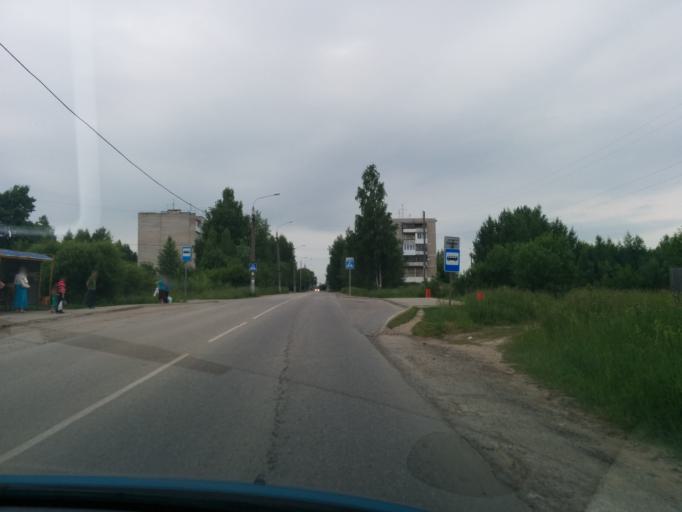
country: RU
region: Perm
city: Perm
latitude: 58.1577
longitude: 56.3051
